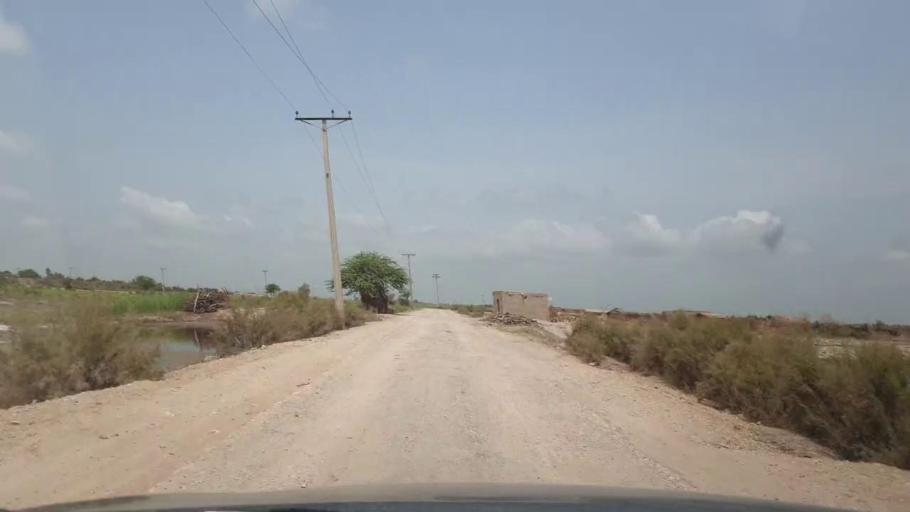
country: PK
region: Sindh
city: Ratodero
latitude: 27.9081
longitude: 68.3099
